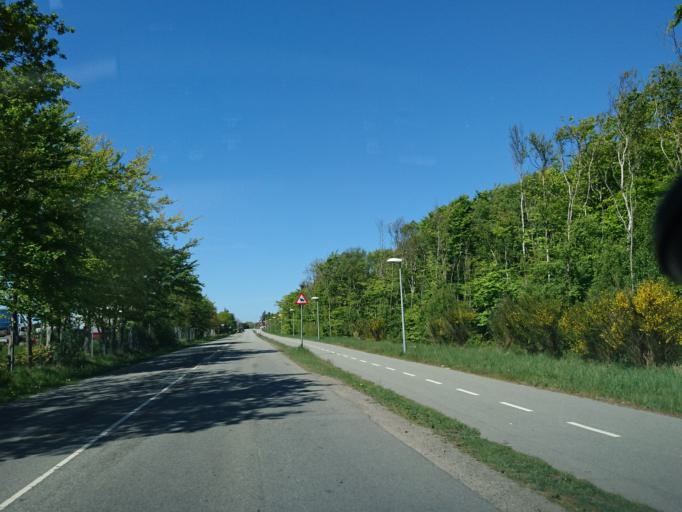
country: DK
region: North Denmark
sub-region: Hjorring Kommune
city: Hirtshals
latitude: 57.5774
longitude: 9.9836
